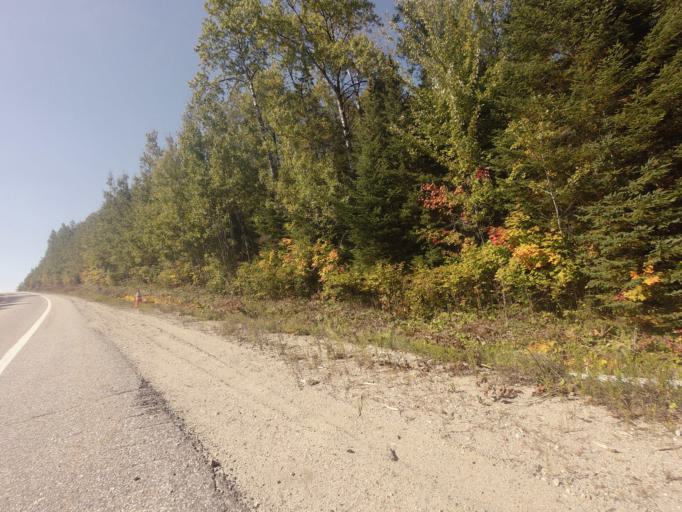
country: CA
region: Quebec
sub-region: Outaouais
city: Maniwaki
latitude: 46.5561
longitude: -75.7907
